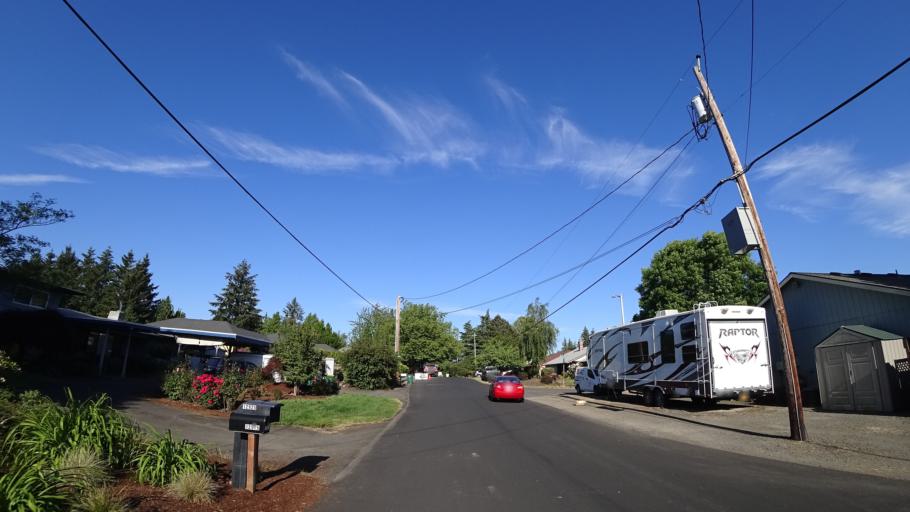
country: US
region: Oregon
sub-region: Washington County
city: Beaverton
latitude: 45.4602
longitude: -122.8105
